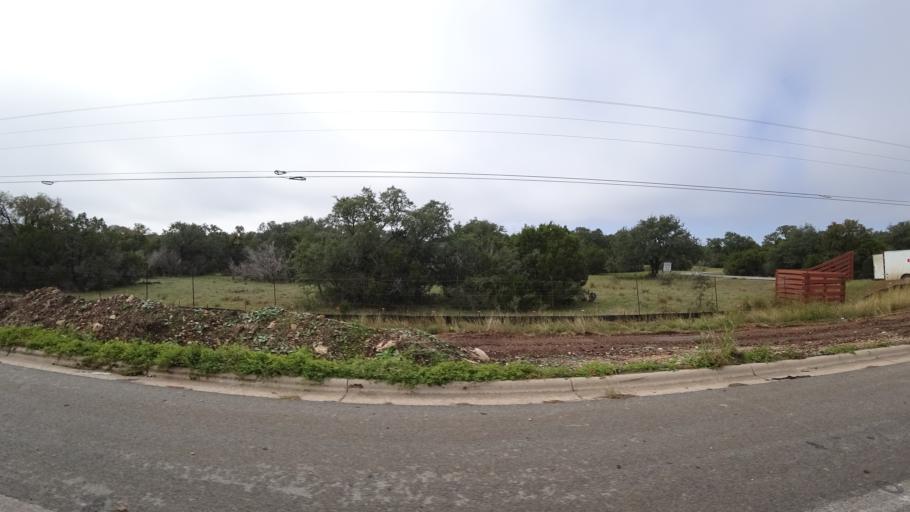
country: US
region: Texas
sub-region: Travis County
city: Shady Hollow
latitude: 30.1760
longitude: -97.8927
